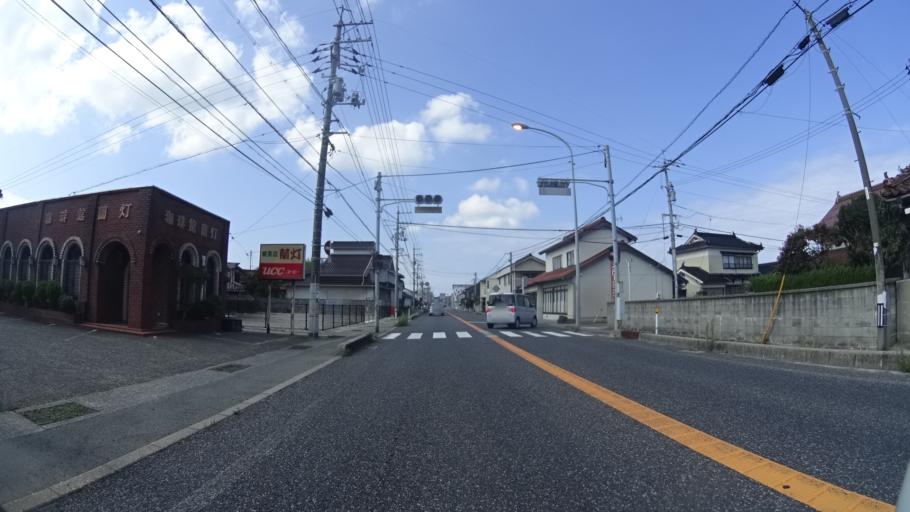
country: JP
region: Shimane
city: Gotsucho
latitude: 35.0066
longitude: 132.2121
